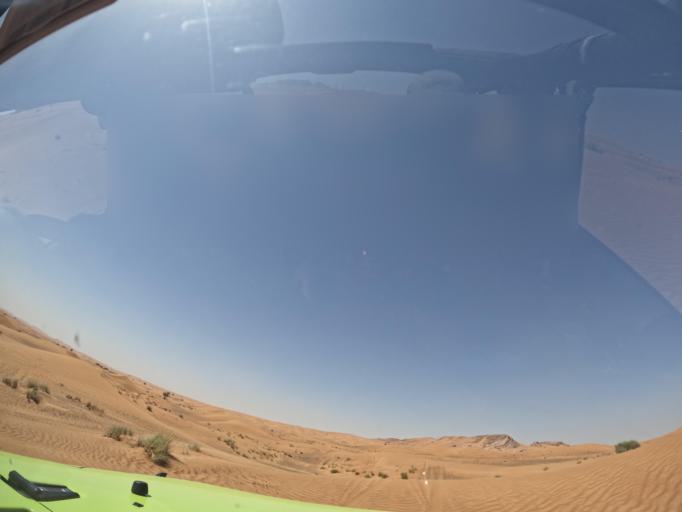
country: AE
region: Ash Shariqah
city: Adh Dhayd
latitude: 25.0191
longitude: 55.7440
